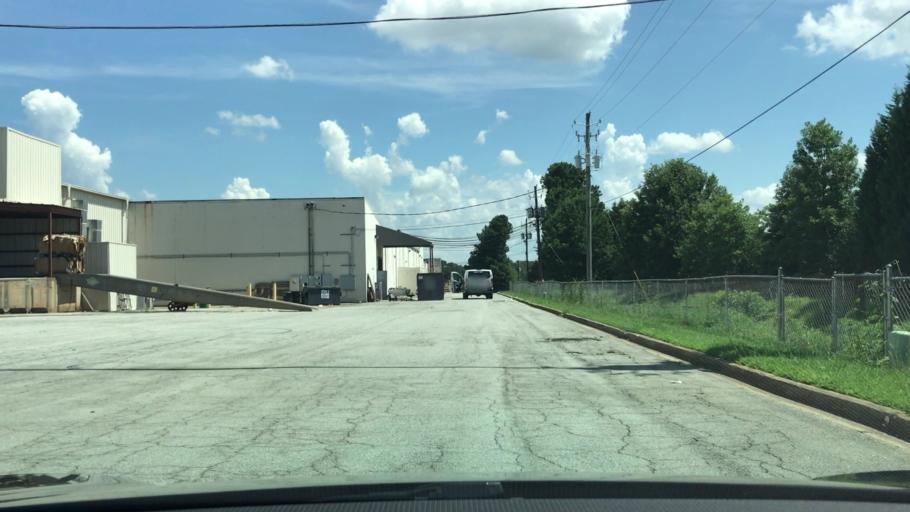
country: US
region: Georgia
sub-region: Gwinnett County
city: Sugar Hill
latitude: 34.0962
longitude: -84.0169
